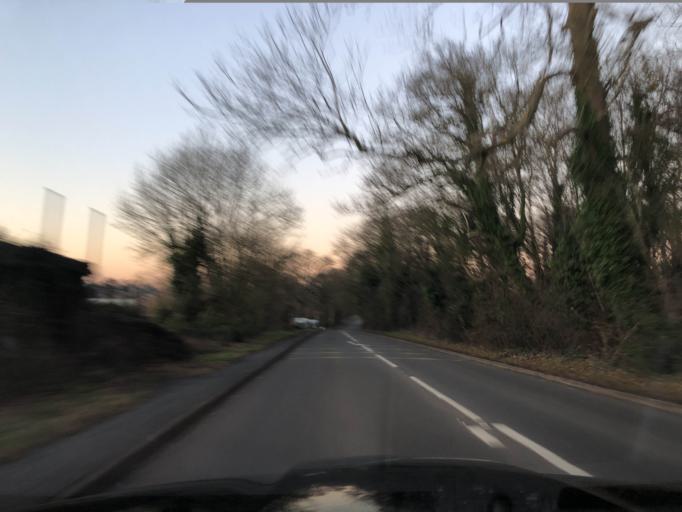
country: GB
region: England
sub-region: Warwickshire
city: Kenilworth
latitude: 52.3220
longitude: -1.5760
